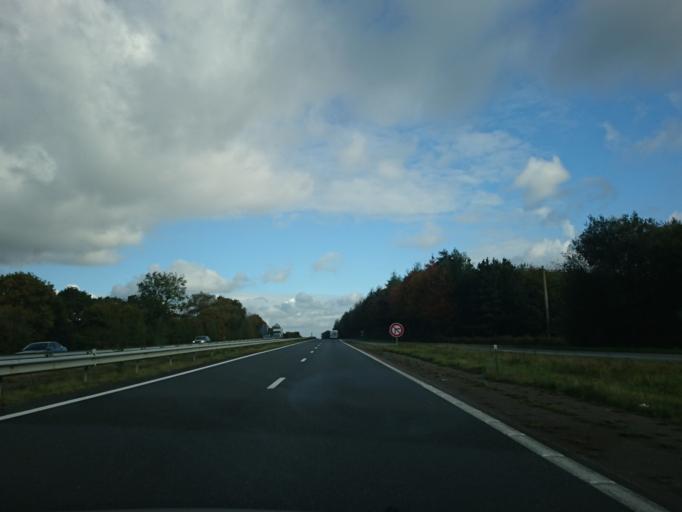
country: FR
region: Brittany
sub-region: Departement des Cotes-d'Armor
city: Pedernec
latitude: 48.5674
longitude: -3.2385
